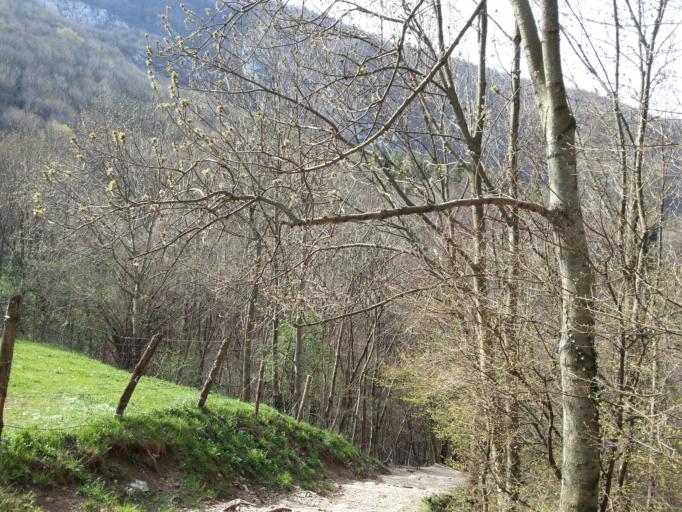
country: IT
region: Lombardy
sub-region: Provincia di Como
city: Valbrona
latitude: 45.8562
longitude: 9.3129
